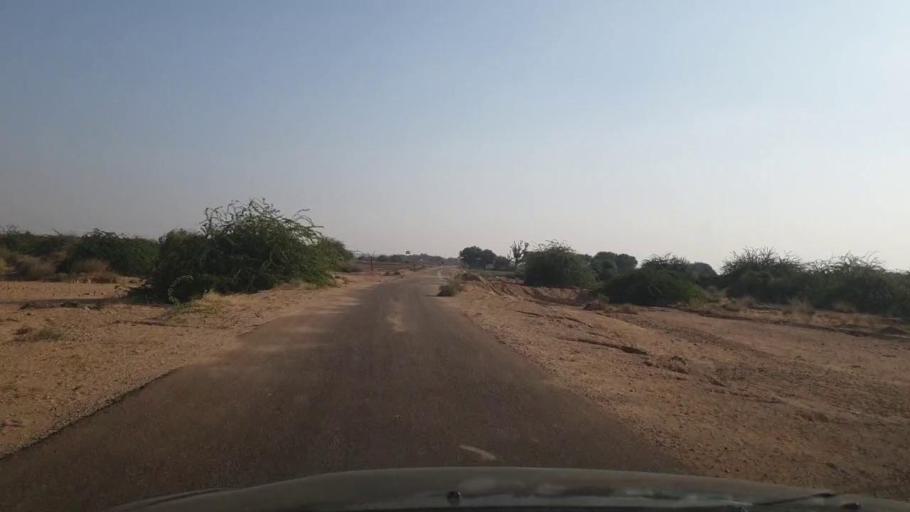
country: PK
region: Sindh
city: Jamshoro
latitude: 25.3356
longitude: 67.8423
